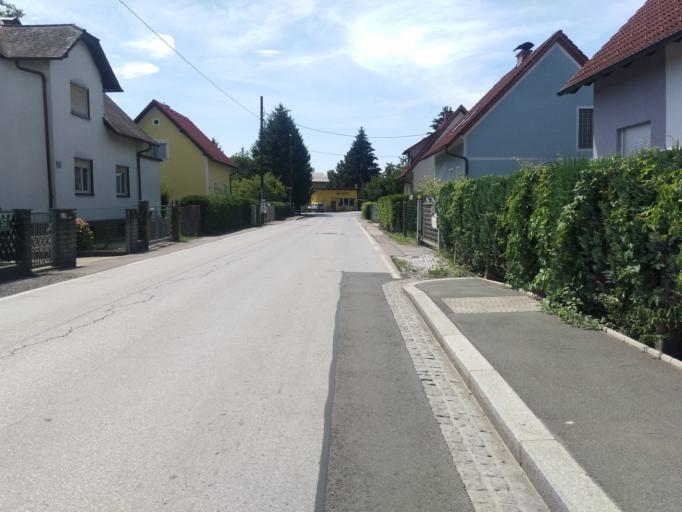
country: AT
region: Styria
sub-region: Politischer Bezirk Graz-Umgebung
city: Feldkirchen bei Graz
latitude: 47.0266
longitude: 15.4416
